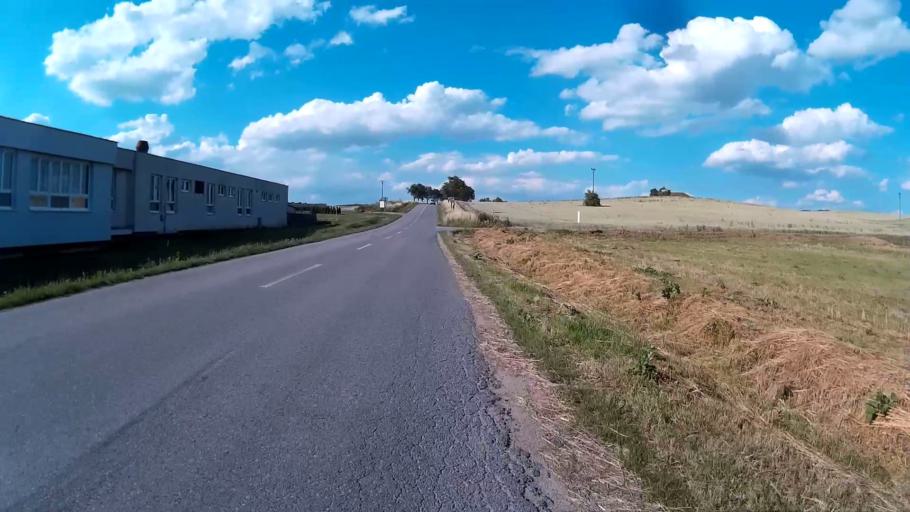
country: CZ
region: South Moravian
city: Sitborice
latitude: 49.0196
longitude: 16.7769
